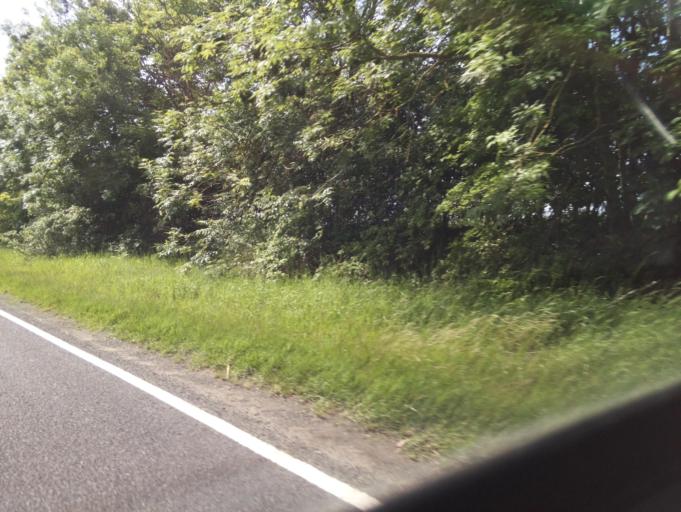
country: GB
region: England
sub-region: Lincolnshire
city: Burton
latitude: 53.3283
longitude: -0.5416
